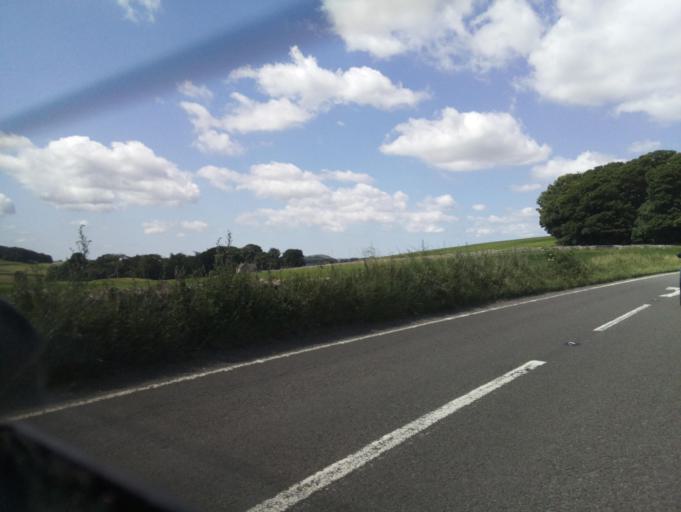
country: GB
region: England
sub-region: Derbyshire
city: Ashbourne
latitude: 53.0902
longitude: -1.7693
